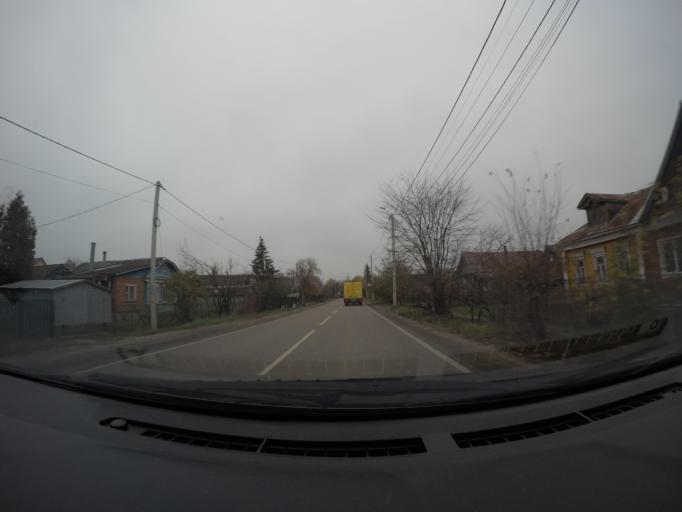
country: RU
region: Moskovskaya
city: Gzhel'
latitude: 55.5812
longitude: 38.4005
